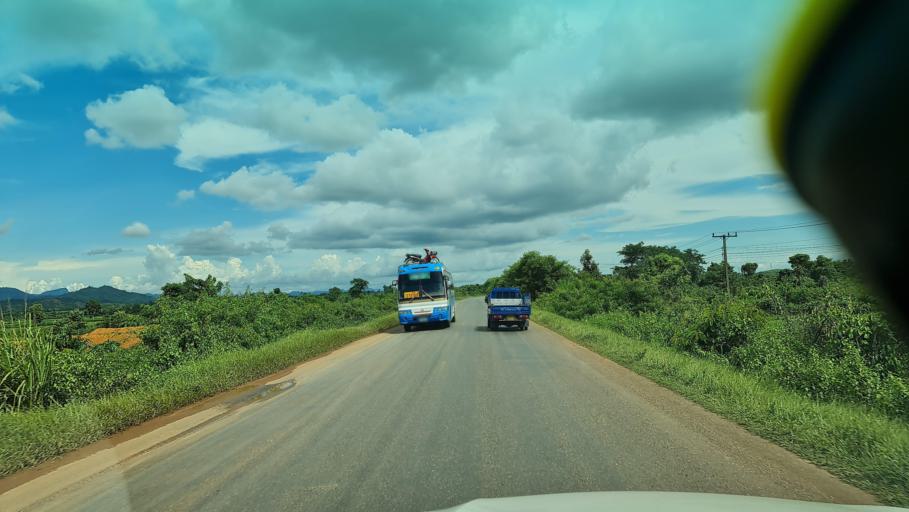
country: LA
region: Bolikhamxai
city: Ban Nahin
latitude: 18.1869
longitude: 104.2254
